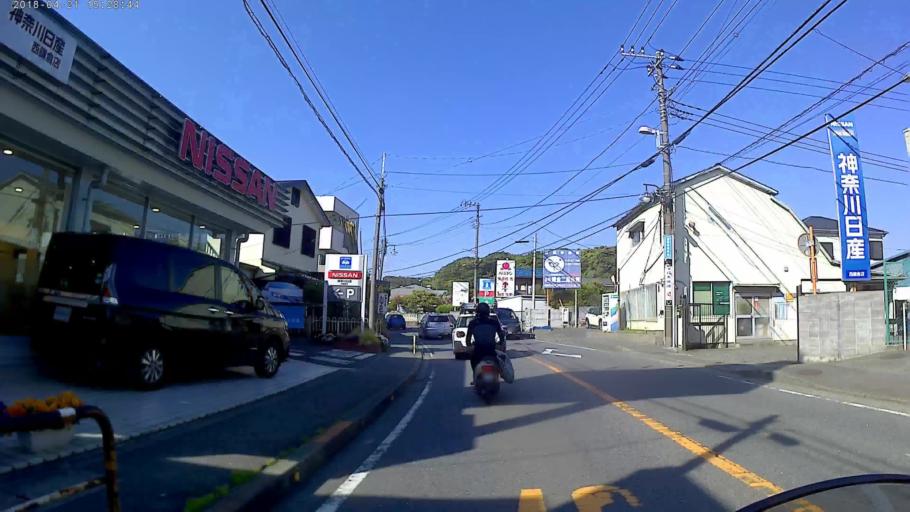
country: JP
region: Kanagawa
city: Fujisawa
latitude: 35.3158
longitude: 139.5027
